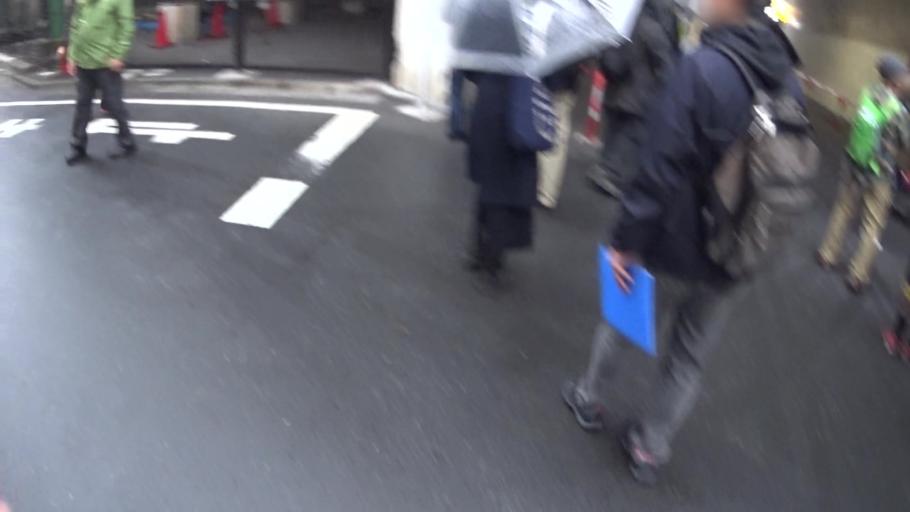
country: JP
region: Tokyo
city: Tokyo
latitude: 35.6926
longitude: 139.7230
